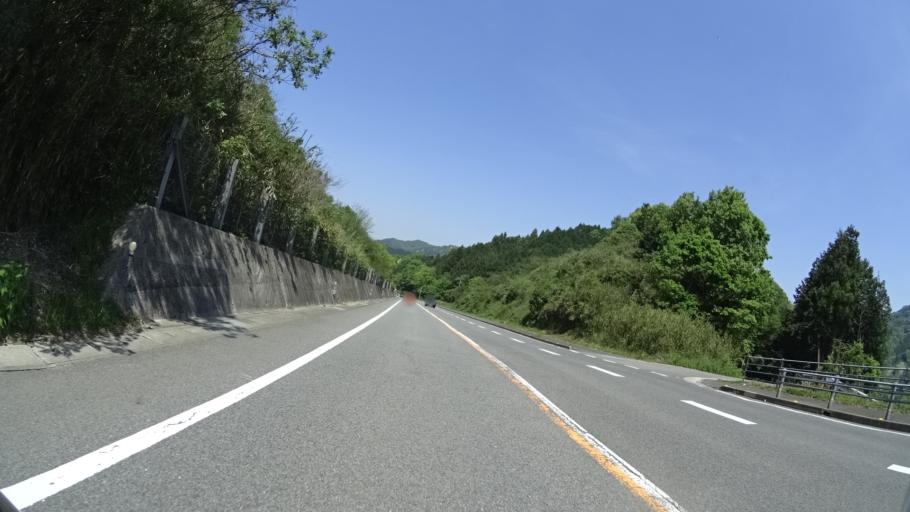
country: JP
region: Ehime
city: Hojo
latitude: 33.9968
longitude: 132.9333
